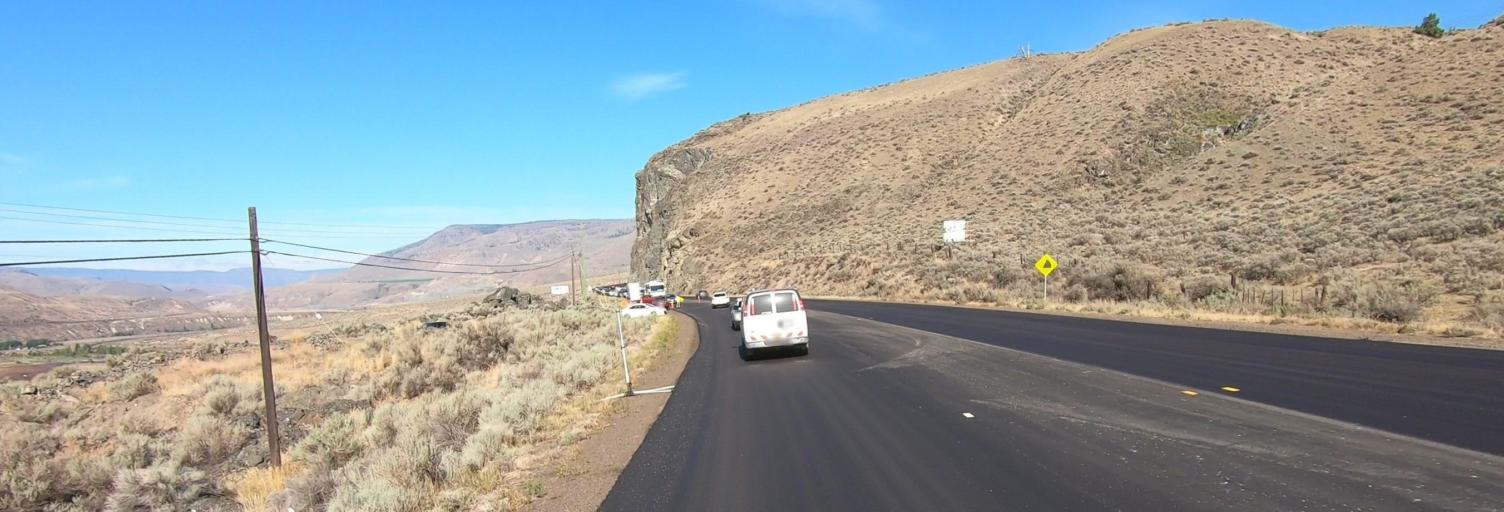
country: CA
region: British Columbia
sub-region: Thompson-Nicola Regional District
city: Ashcroft
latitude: 50.7808
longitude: -121.0559
